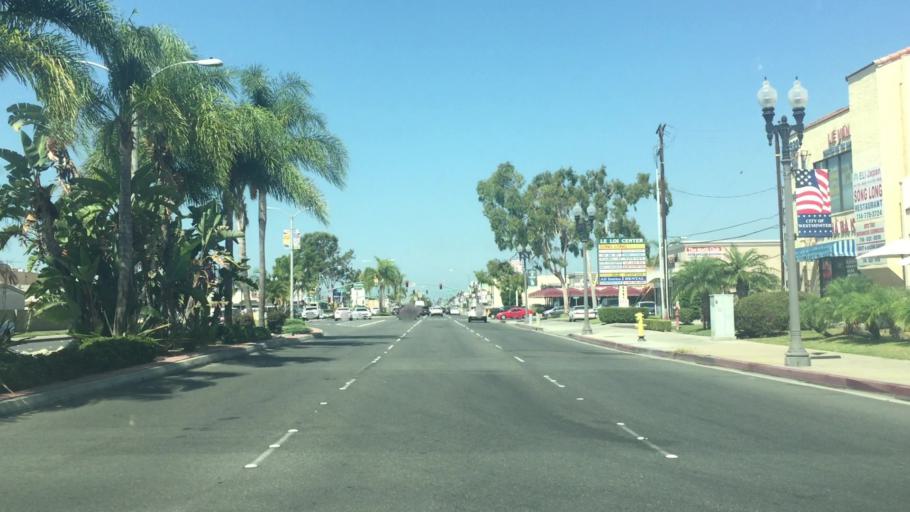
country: US
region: California
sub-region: Orange County
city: Midway City
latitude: 33.7450
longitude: -117.9651
